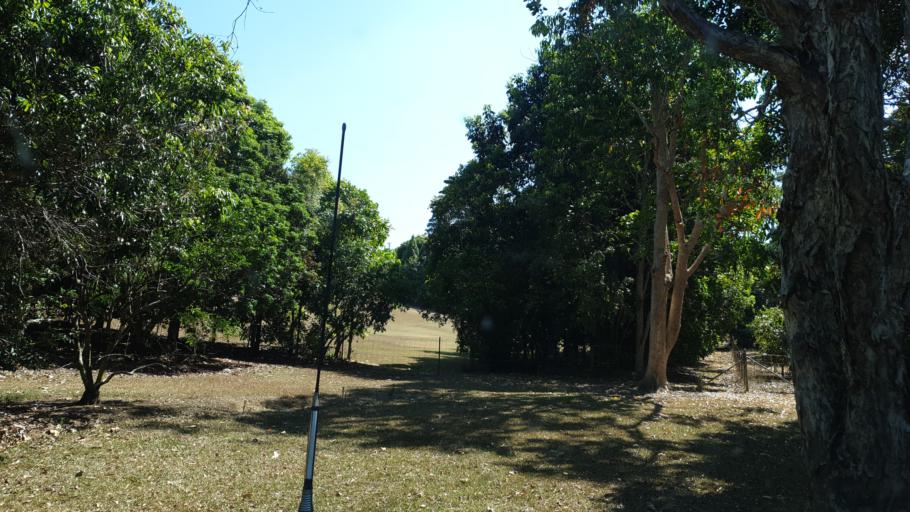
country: AU
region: Queensland
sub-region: Tablelands
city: Tolga
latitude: -17.2171
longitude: 145.6143
